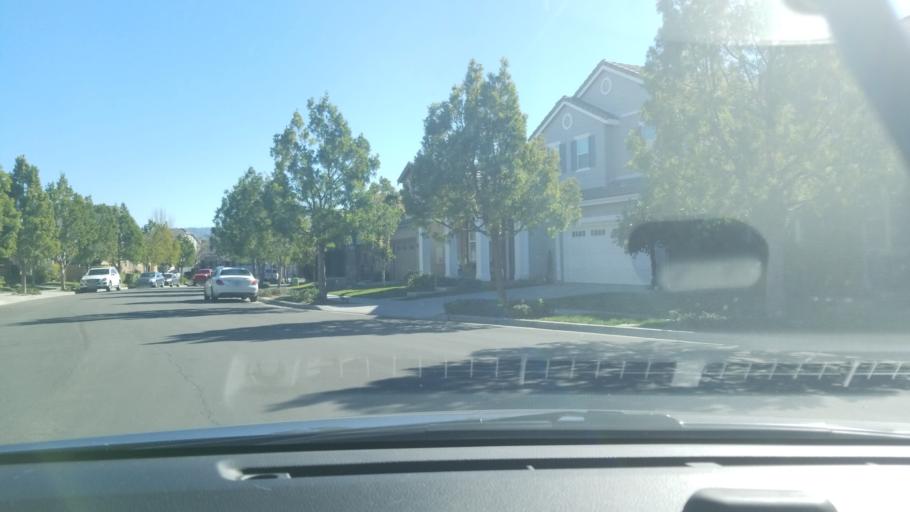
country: US
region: California
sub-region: Riverside County
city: Murrieta Hot Springs
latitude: 33.5364
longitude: -117.1638
